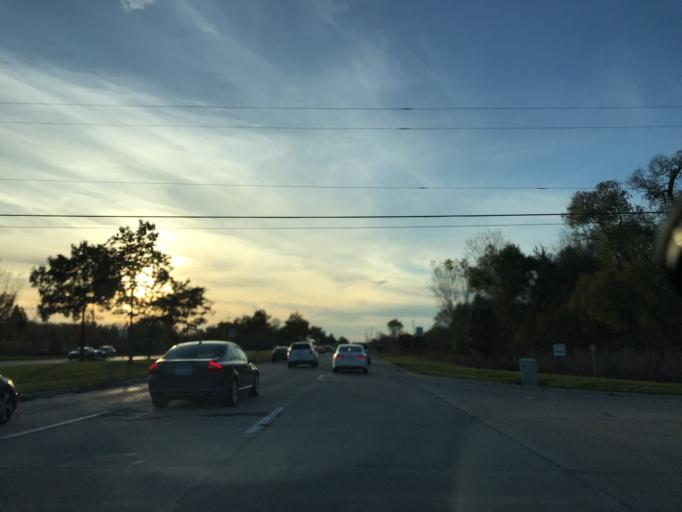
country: US
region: Michigan
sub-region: Oakland County
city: Novi
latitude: 42.4966
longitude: -83.4502
